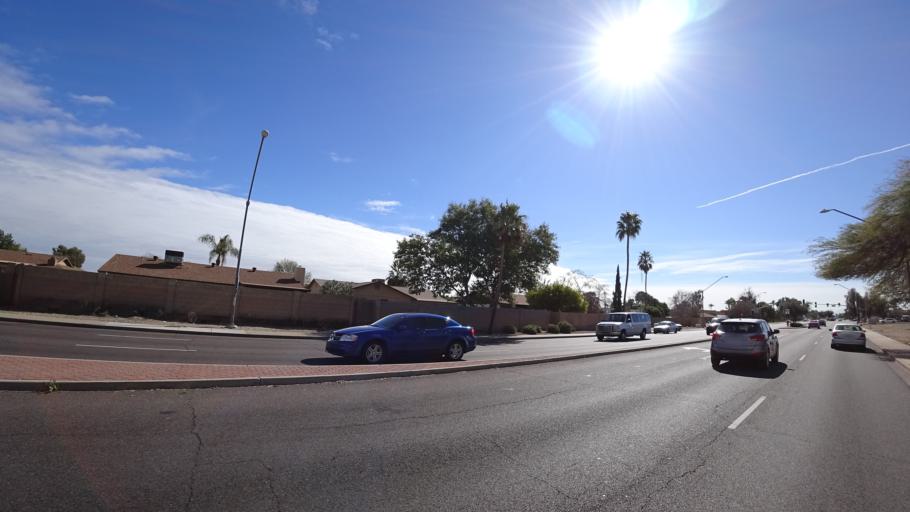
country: US
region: Arizona
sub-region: Maricopa County
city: Glendale
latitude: 33.5862
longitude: -112.1862
